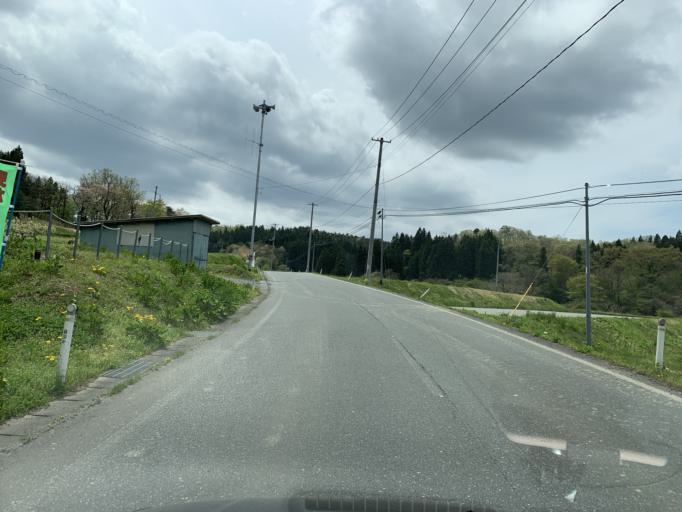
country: JP
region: Iwate
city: Ichinoseki
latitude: 38.8554
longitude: 141.3334
